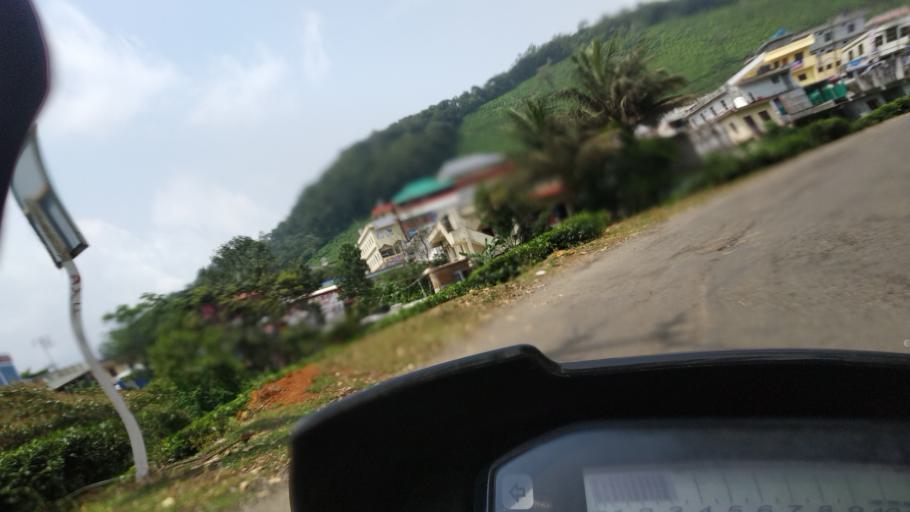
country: IN
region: Kerala
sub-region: Kottayam
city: Erattupetta
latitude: 9.6297
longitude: 76.9781
